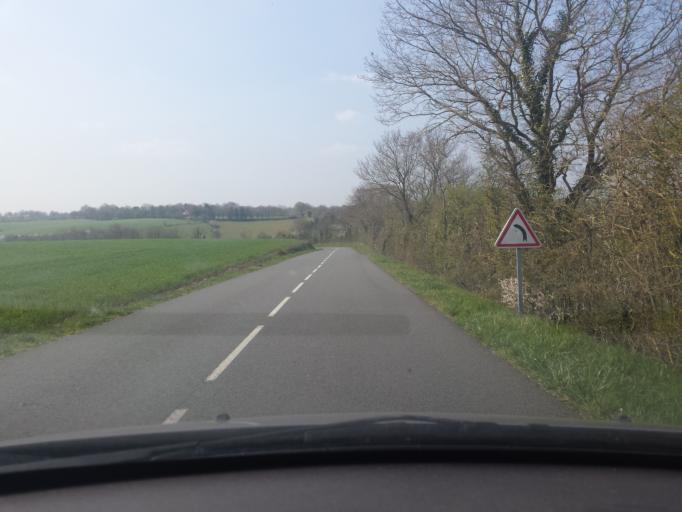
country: FR
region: Pays de la Loire
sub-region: Departement de la Vendee
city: Bournezeau
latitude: 46.6732
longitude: -1.1828
